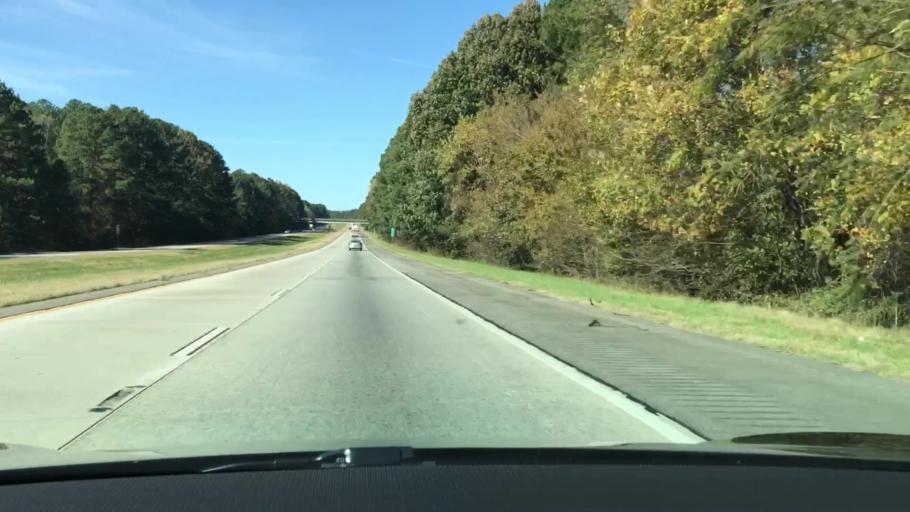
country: US
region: Georgia
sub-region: Greene County
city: Union Point
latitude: 33.5477
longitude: -83.0384
